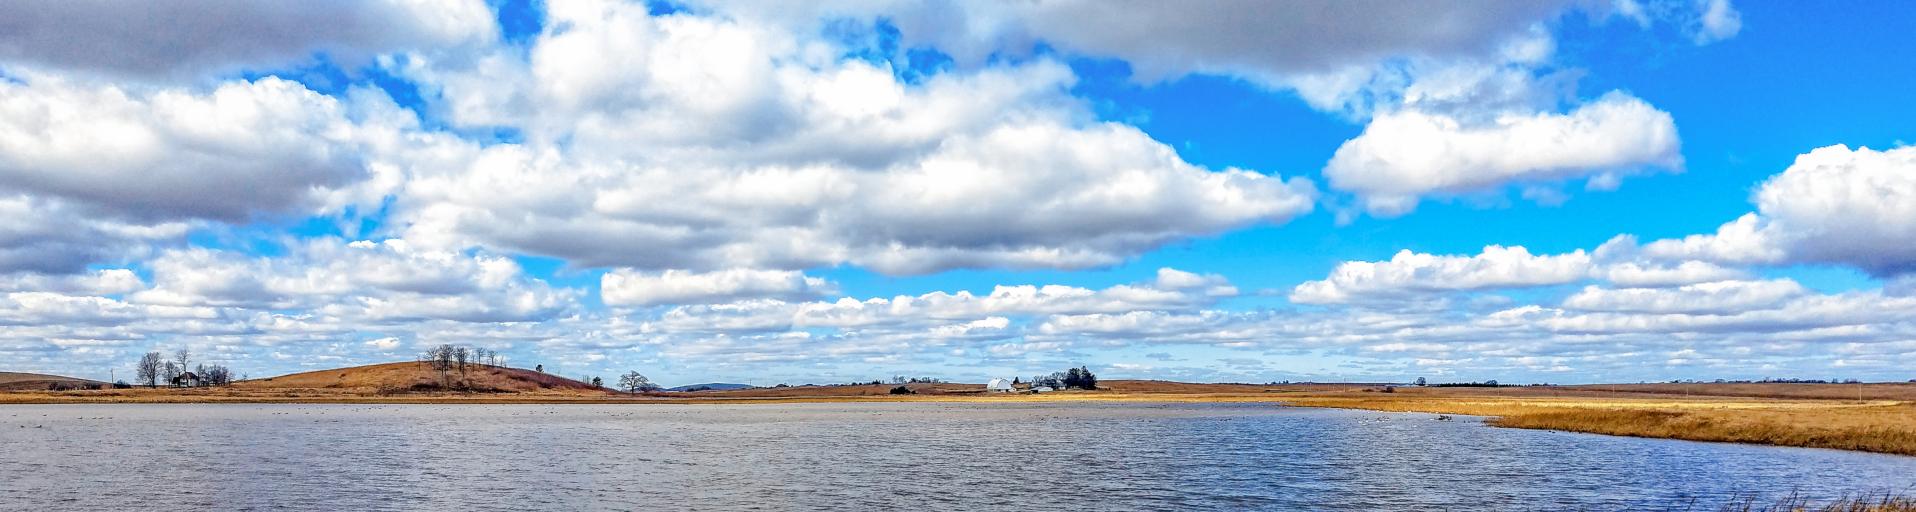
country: US
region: Wisconsin
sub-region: Dane County
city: De Forest
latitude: 43.3186
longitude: -89.3628
